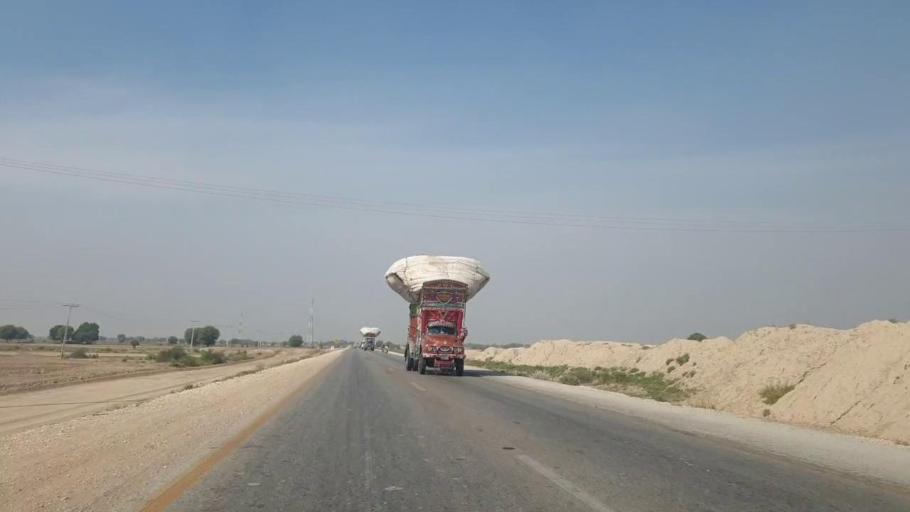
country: PK
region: Sindh
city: Sann
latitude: 25.9754
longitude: 68.1864
